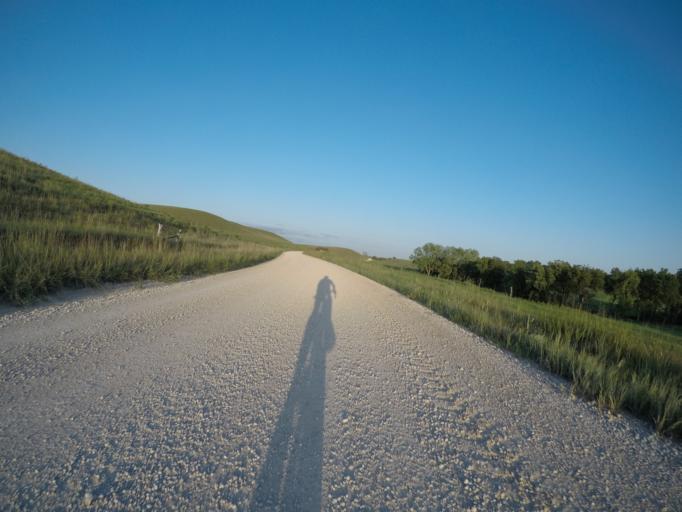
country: US
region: Kansas
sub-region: Riley County
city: Ogden
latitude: 39.0124
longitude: -96.6539
